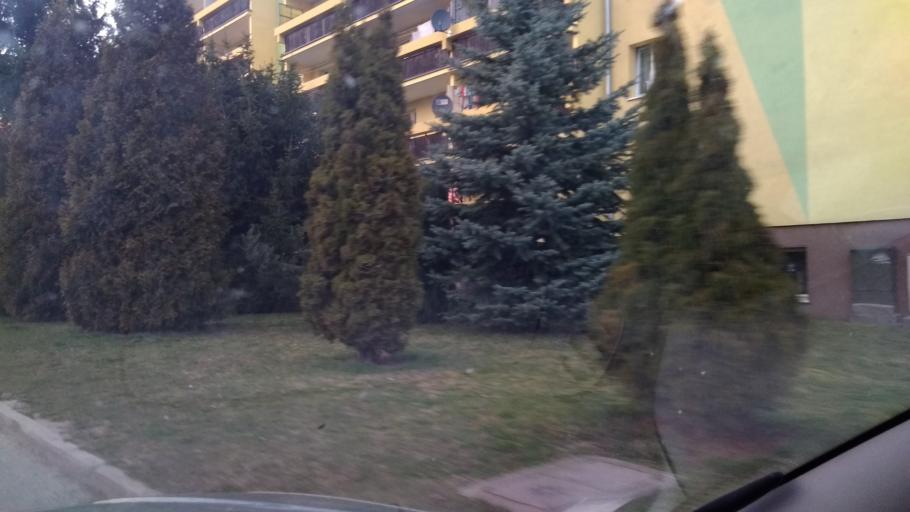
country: PL
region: Lower Silesian Voivodeship
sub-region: Powiat jeleniogorski
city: Jezow Sudecki
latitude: 50.9220
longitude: 15.7587
